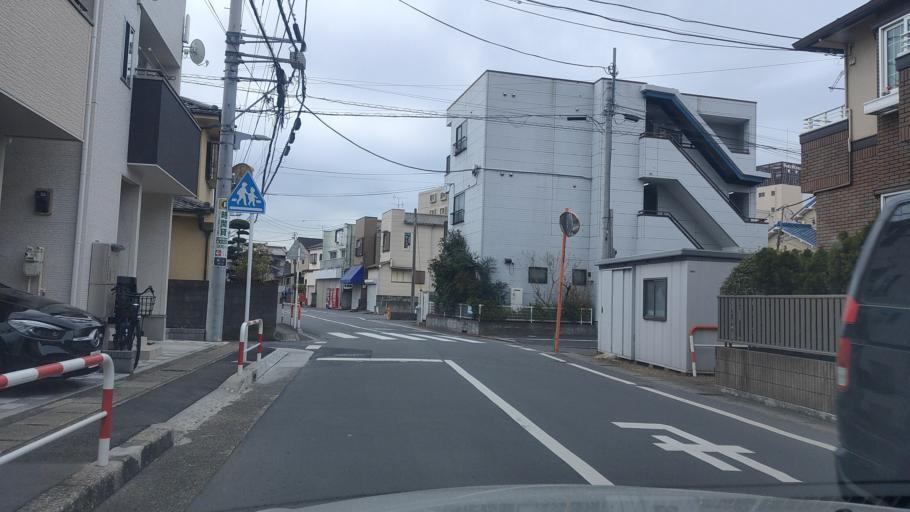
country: JP
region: Tokyo
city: Urayasu
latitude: 35.6624
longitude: 139.8892
